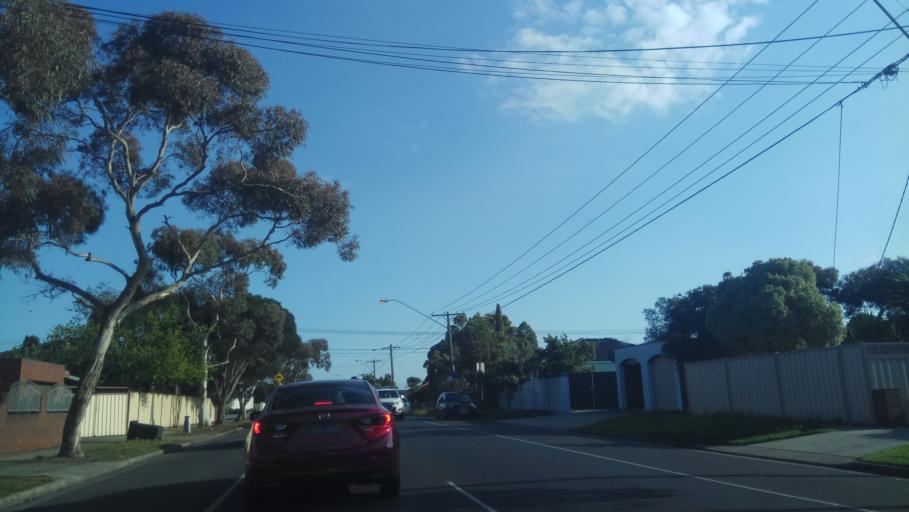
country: AU
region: Victoria
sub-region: Hobsons Bay
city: Laverton
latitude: -37.8680
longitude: 144.7781
